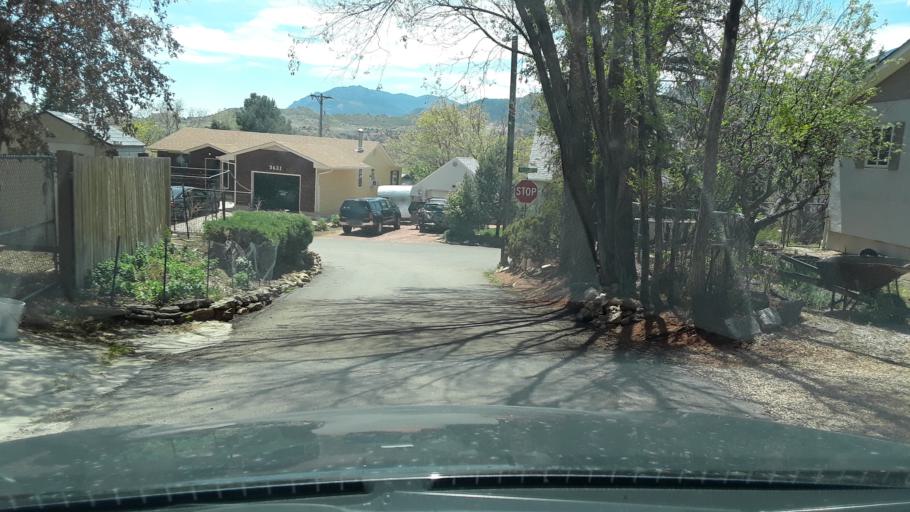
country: US
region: Colorado
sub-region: El Paso County
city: Manitou Springs
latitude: 38.8608
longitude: -104.8827
